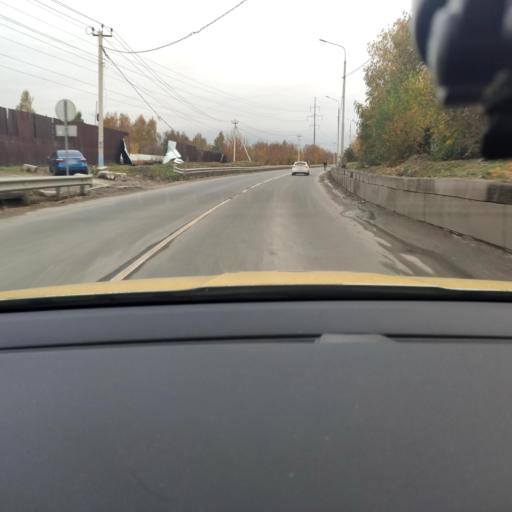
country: RU
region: Moskovskaya
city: Mosrentgen
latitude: 55.6088
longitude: 37.4584
